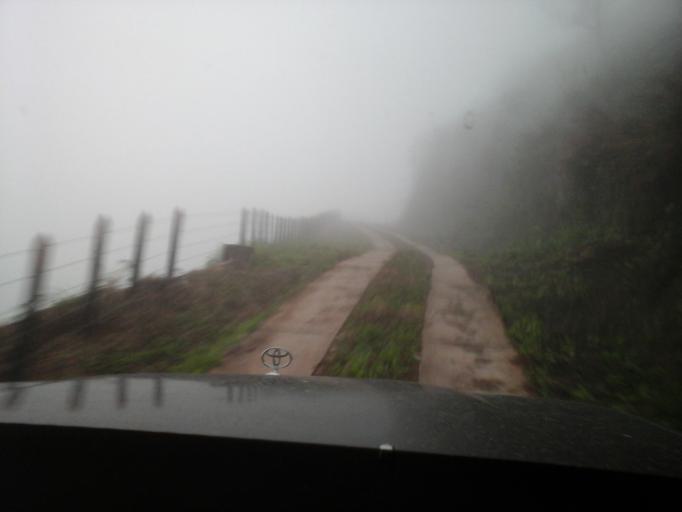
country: CO
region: Cesar
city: Agustin Codazzi
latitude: 9.9426
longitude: -73.1255
